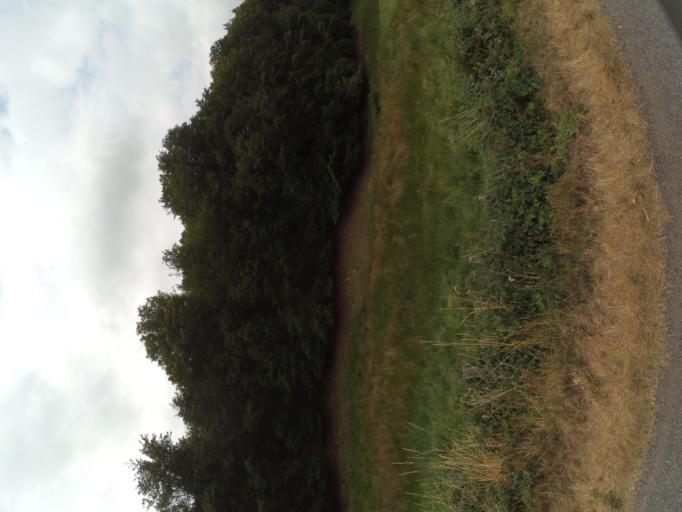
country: FR
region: Limousin
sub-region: Departement de la Correze
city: Meymac
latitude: 45.6554
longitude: 2.1093
